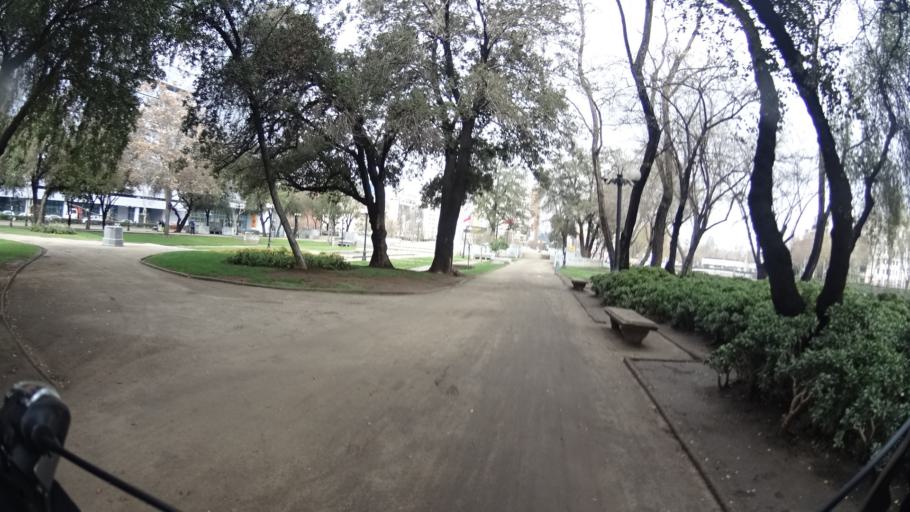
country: CL
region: Santiago Metropolitan
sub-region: Provincia de Santiago
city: Santiago
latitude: -33.4359
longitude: -70.6321
